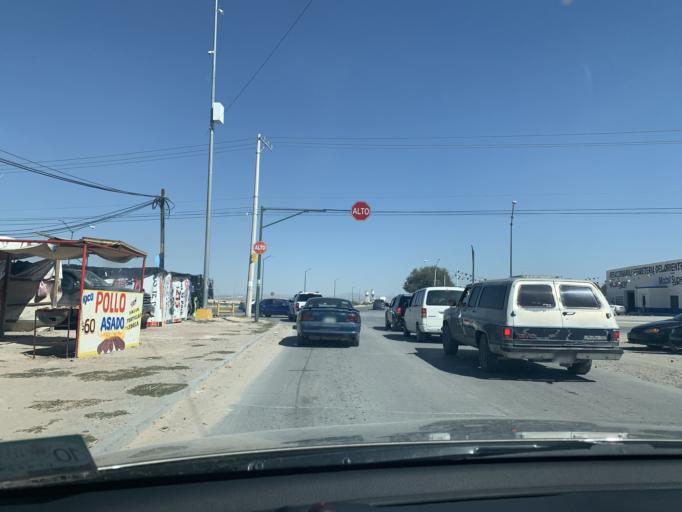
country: US
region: Texas
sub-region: El Paso County
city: Socorro Mission Number 1 Colonia
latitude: 31.6051
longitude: -106.3528
